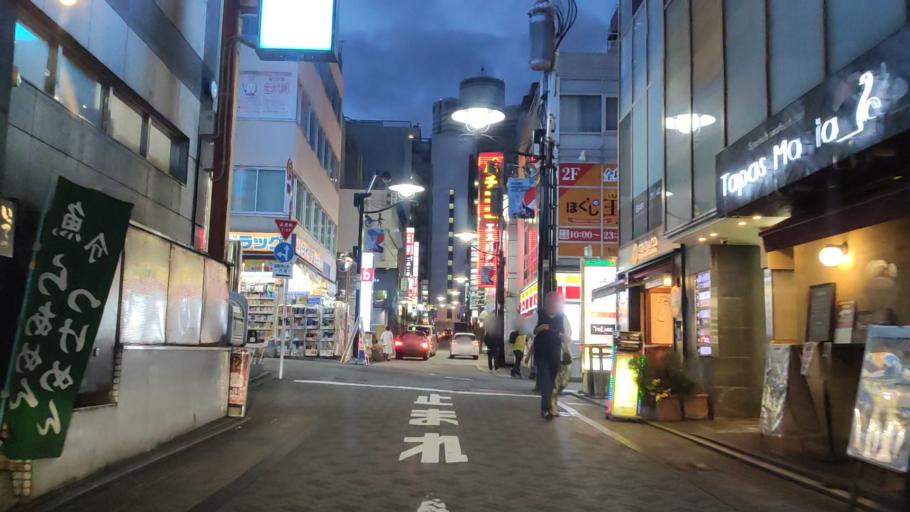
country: JP
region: Tokyo
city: Tokyo
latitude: 35.6762
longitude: 139.7364
